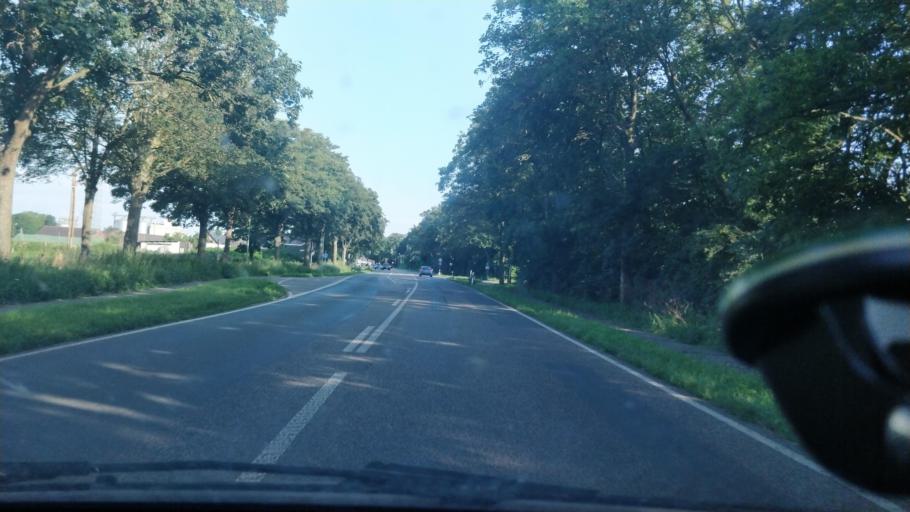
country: DE
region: North Rhine-Westphalia
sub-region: Regierungsbezirk Dusseldorf
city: Kamp-Lintfort
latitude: 51.5176
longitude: 6.5350
